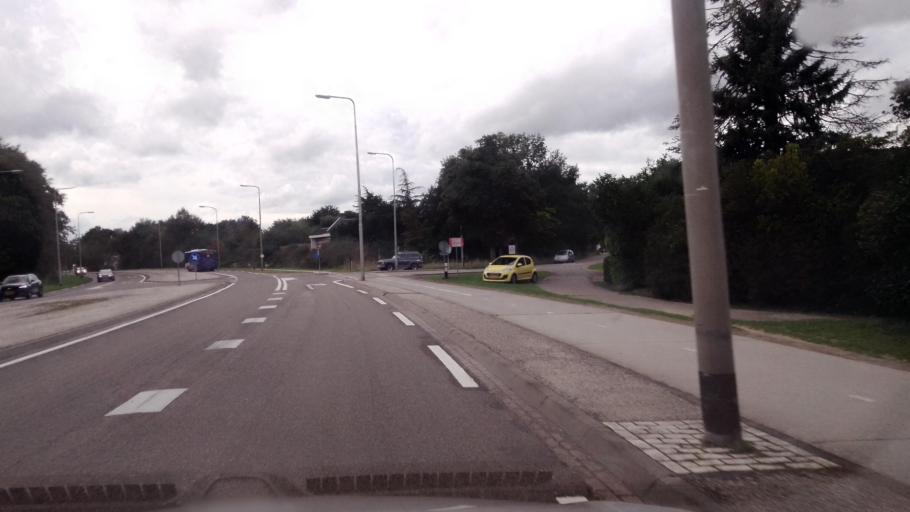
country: NL
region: Limburg
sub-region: Gemeente Peel en Maas
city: Maasbree
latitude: 51.3639
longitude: 6.0805
